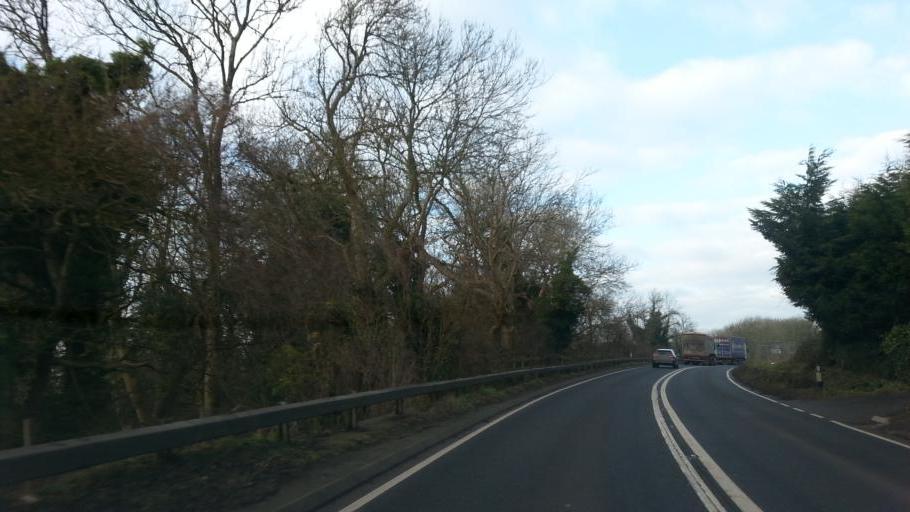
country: GB
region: England
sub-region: South Gloucestershire
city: Cold Ashton
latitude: 51.4252
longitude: -2.3566
